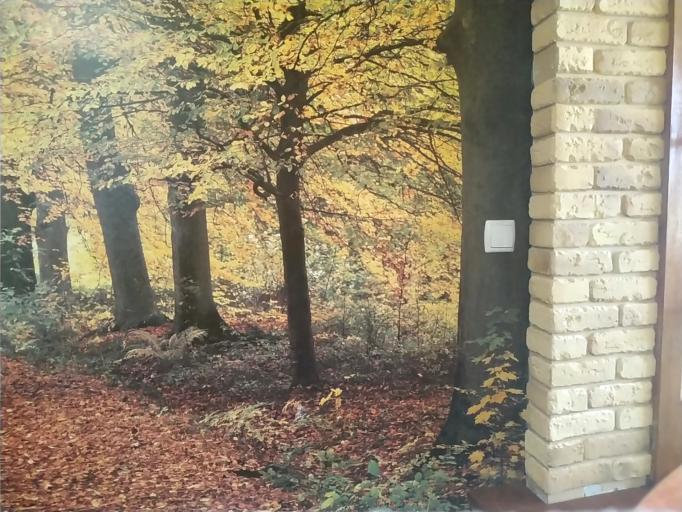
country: RU
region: Tverskaya
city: Vyshniy Volochek
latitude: 57.6467
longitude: 34.5560
